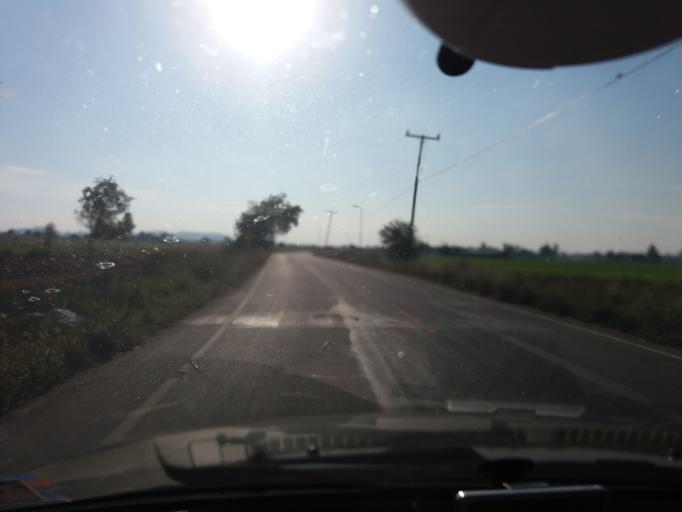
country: TH
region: Suphan Buri
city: Doem Bang Nang Buat
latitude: 14.9153
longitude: 100.1529
